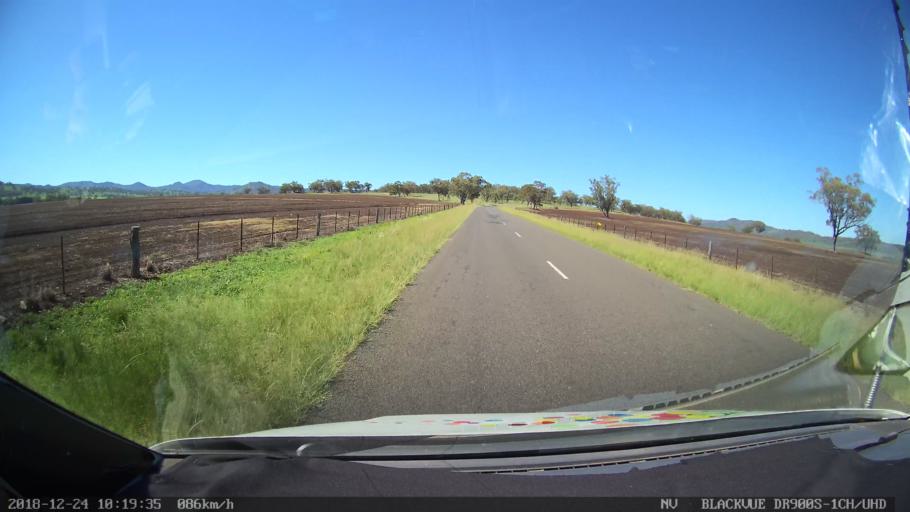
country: AU
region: New South Wales
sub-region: Liverpool Plains
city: Quirindi
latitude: -31.7322
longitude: 150.5648
